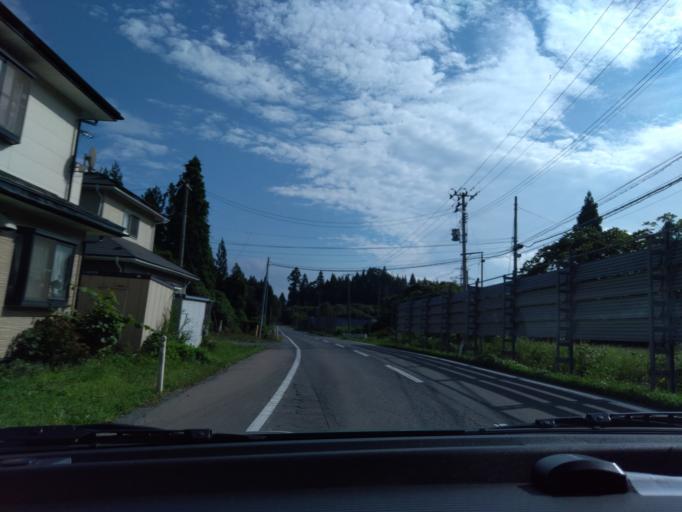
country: JP
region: Iwate
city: Morioka-shi
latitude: 39.6287
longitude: 141.0914
